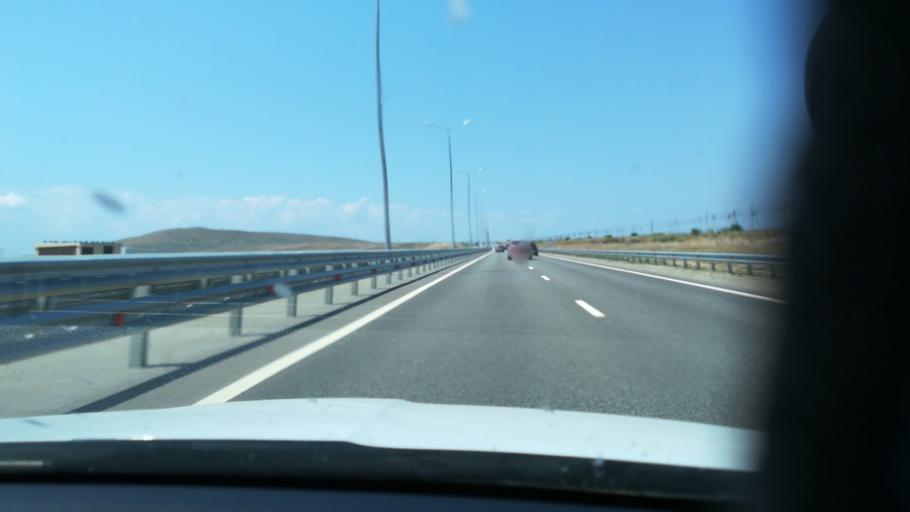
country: RU
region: Krasnodarskiy
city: Vyshestebliyevskaya
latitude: 45.2297
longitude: 36.9073
